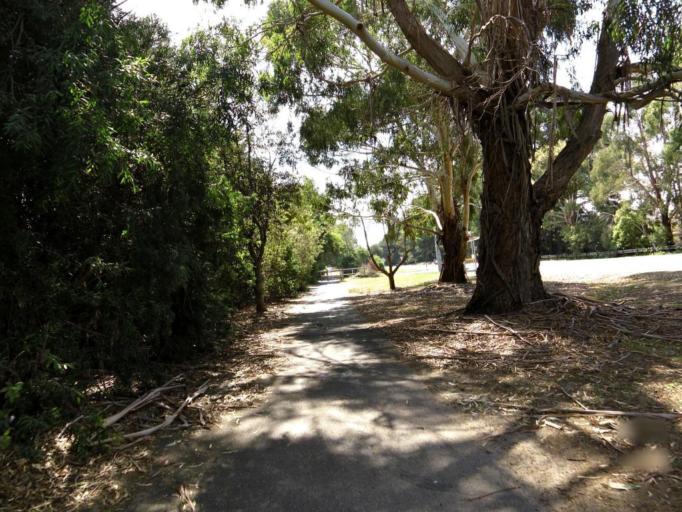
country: AU
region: Victoria
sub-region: Mornington Peninsula
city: Tyabb
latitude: -38.2368
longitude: 145.1875
